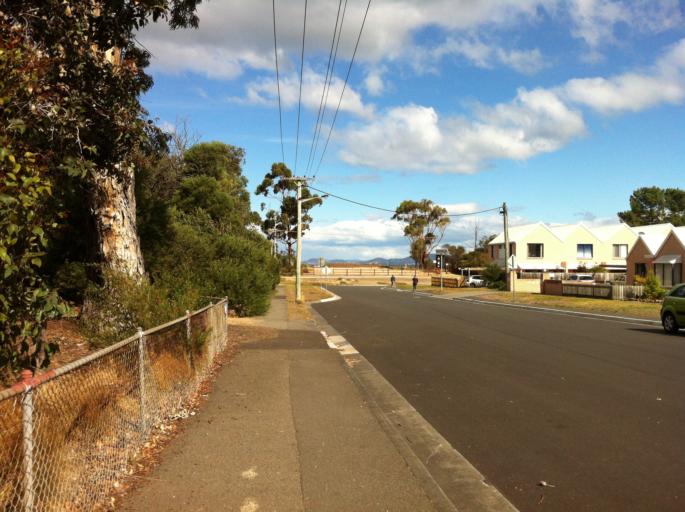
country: AU
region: Tasmania
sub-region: Clarence
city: Bellerive
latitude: -42.8778
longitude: 147.3827
